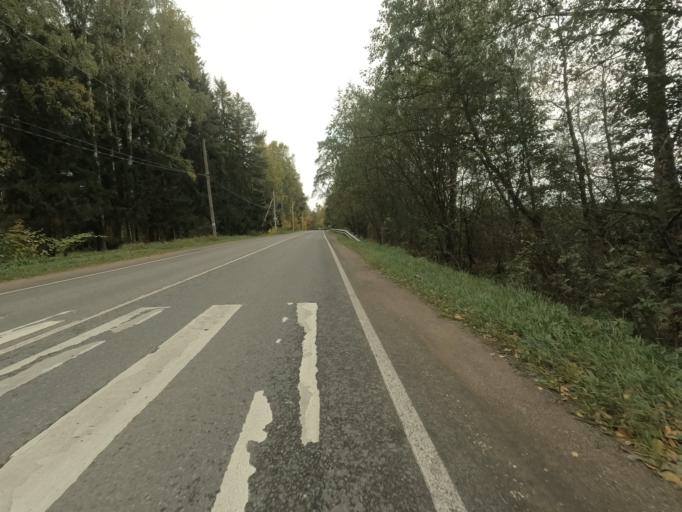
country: RU
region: Leningrad
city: Pavlovo
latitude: 59.7759
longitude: 30.9719
